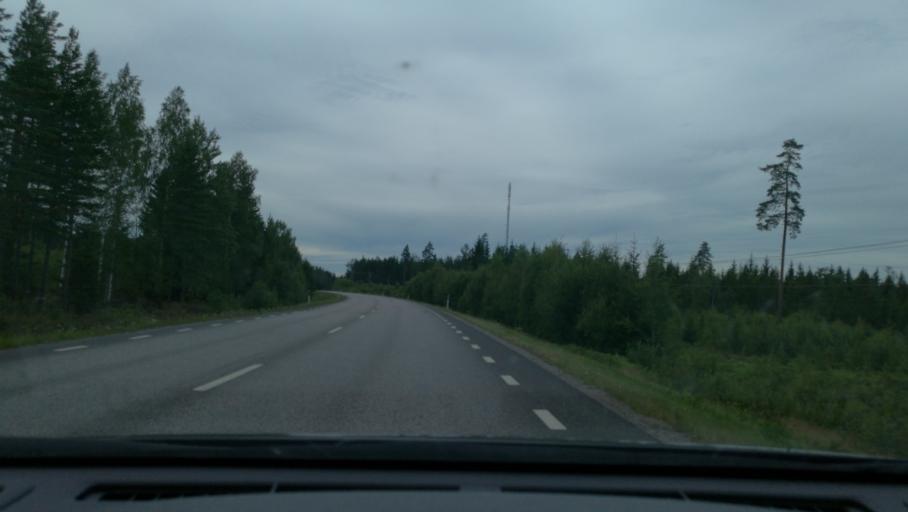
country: SE
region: Soedermanland
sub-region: Katrineholms Kommun
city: Katrineholm
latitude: 59.0816
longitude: 16.2049
